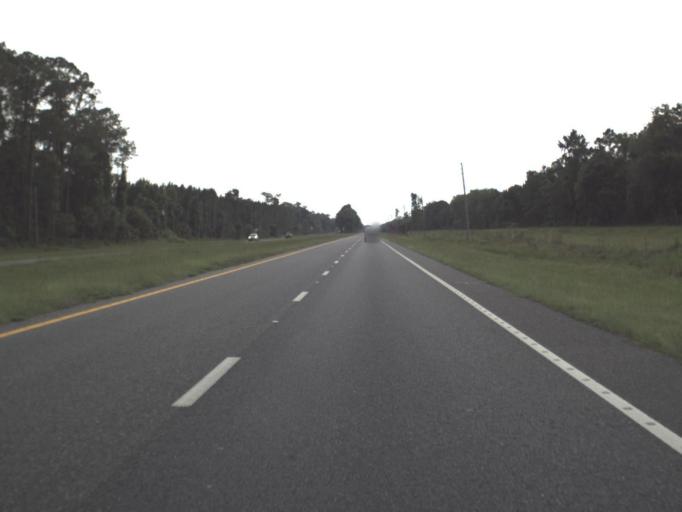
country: US
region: Florida
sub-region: Levy County
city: Inglis
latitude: 29.1679
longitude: -82.6451
